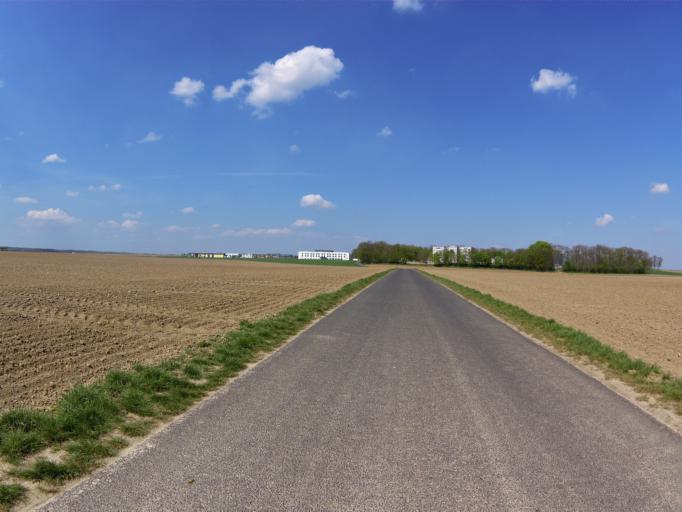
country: DE
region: Bavaria
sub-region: Regierungsbezirk Unterfranken
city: Giebelstadt
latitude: 49.6824
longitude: 9.9509
